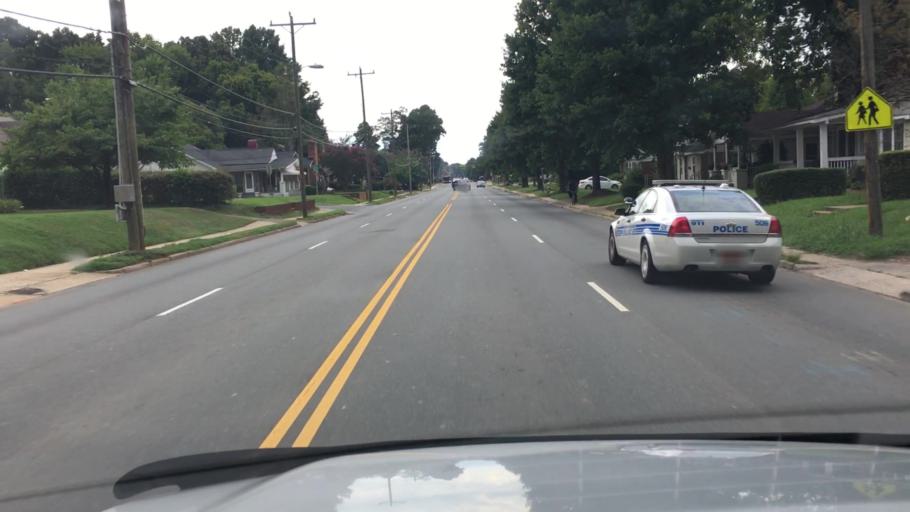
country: US
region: North Carolina
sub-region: Mecklenburg County
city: Charlotte
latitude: 35.2597
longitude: -80.8552
